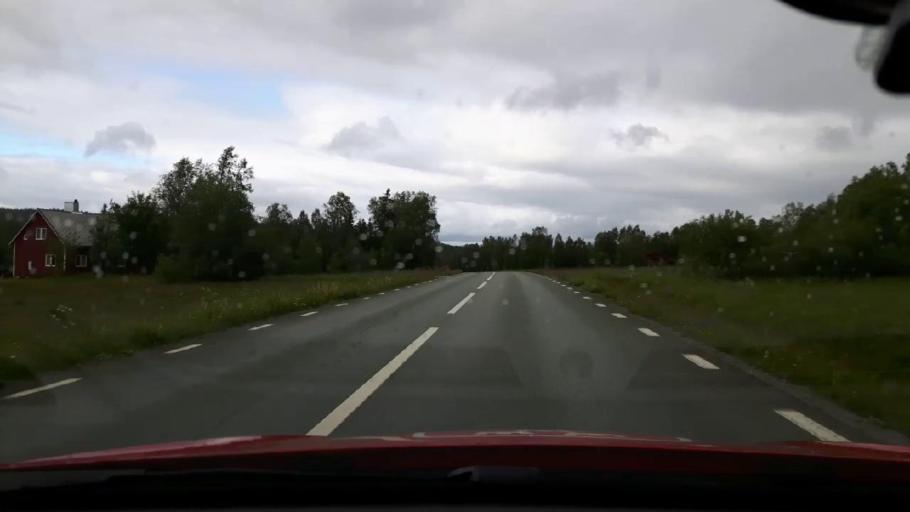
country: SE
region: Jaemtland
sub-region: Are Kommun
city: Are
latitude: 63.3625
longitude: 12.6968
